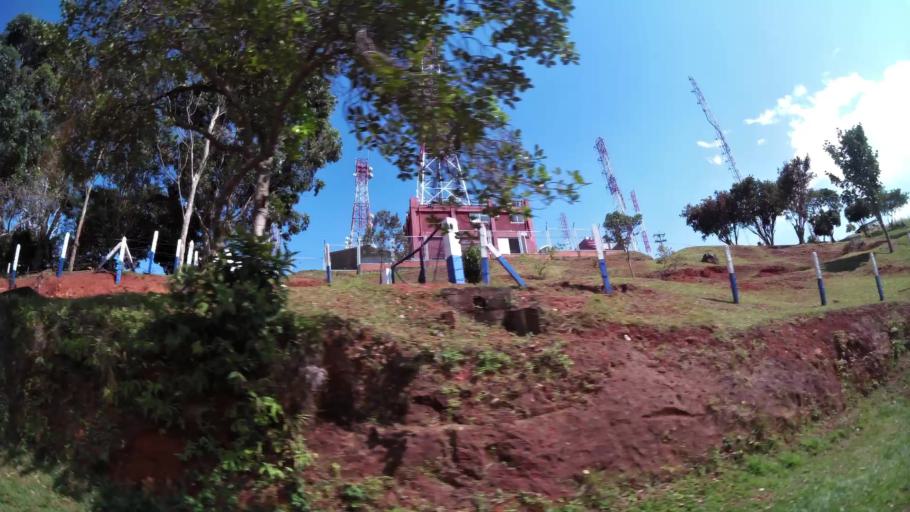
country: CO
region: Valle del Cauca
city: Cali
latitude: 3.4331
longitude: -76.5662
